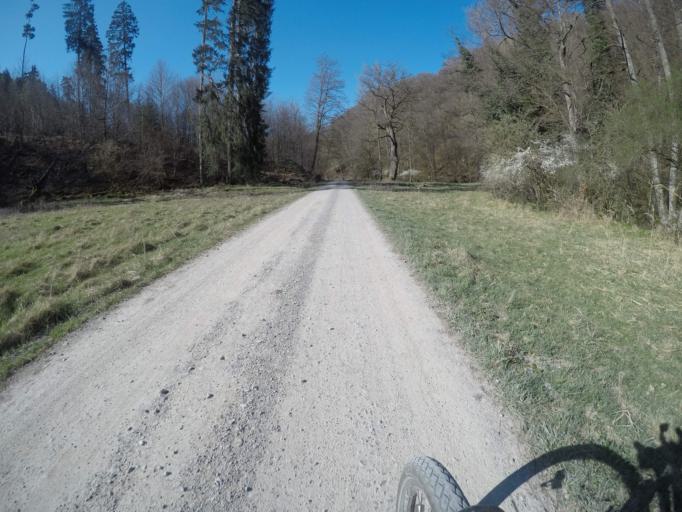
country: DE
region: Baden-Wuerttemberg
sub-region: Regierungsbezirk Stuttgart
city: Weil im Schonbuch
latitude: 48.5800
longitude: 9.0371
